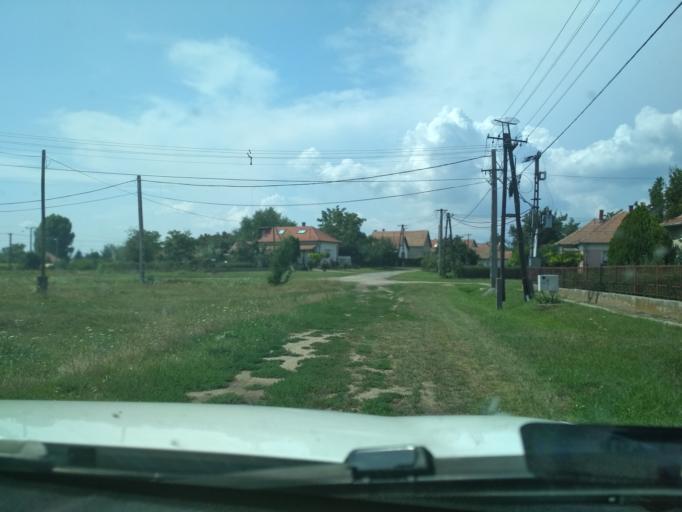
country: HU
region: Jasz-Nagykun-Szolnok
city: Abadszalok
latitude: 47.4685
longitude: 20.5870
